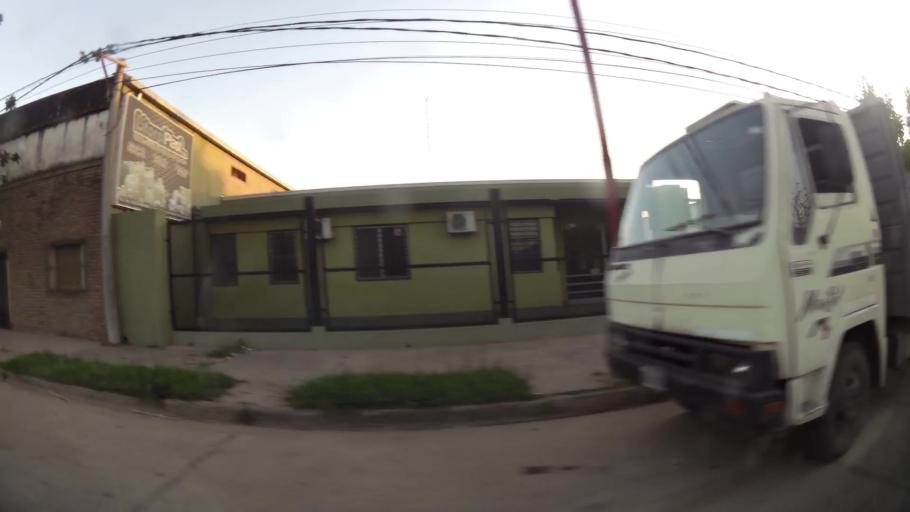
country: AR
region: Santa Fe
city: Santa Fe de la Vera Cruz
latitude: -31.5900
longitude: -60.6954
